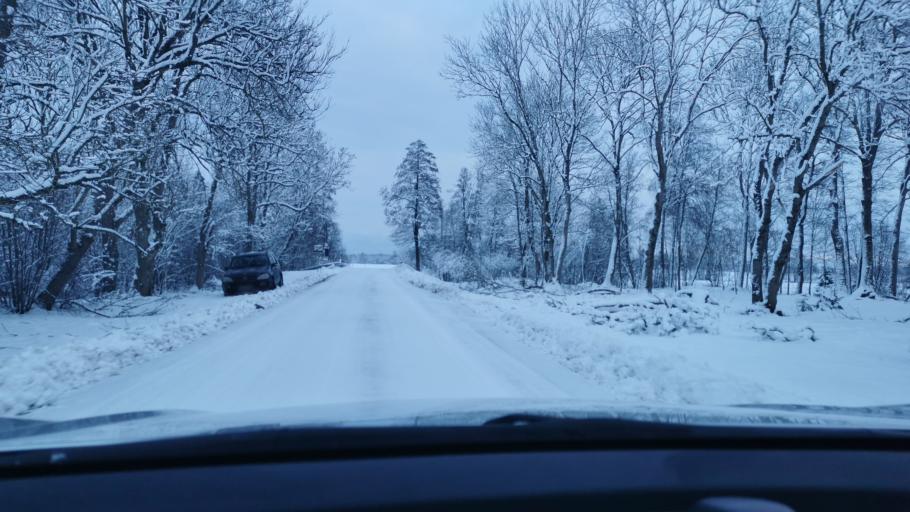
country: EE
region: Laeaene-Virumaa
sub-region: Haljala vald
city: Haljala
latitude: 59.4716
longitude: 26.3504
